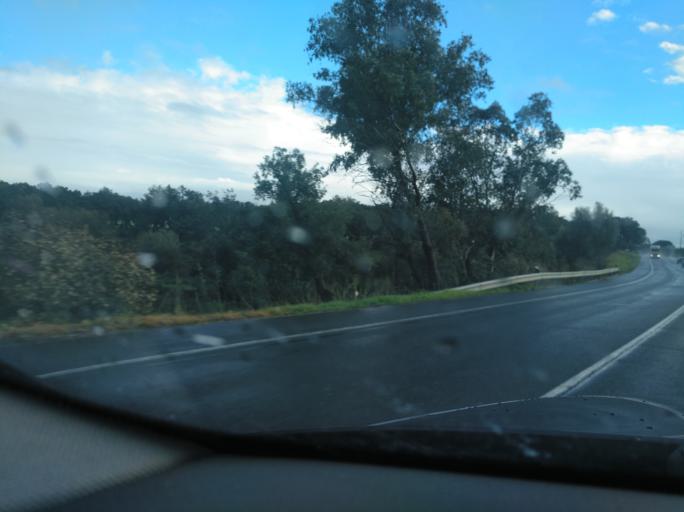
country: PT
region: Setubal
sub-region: Grandola
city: Grandola
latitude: 38.0205
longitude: -8.3989
